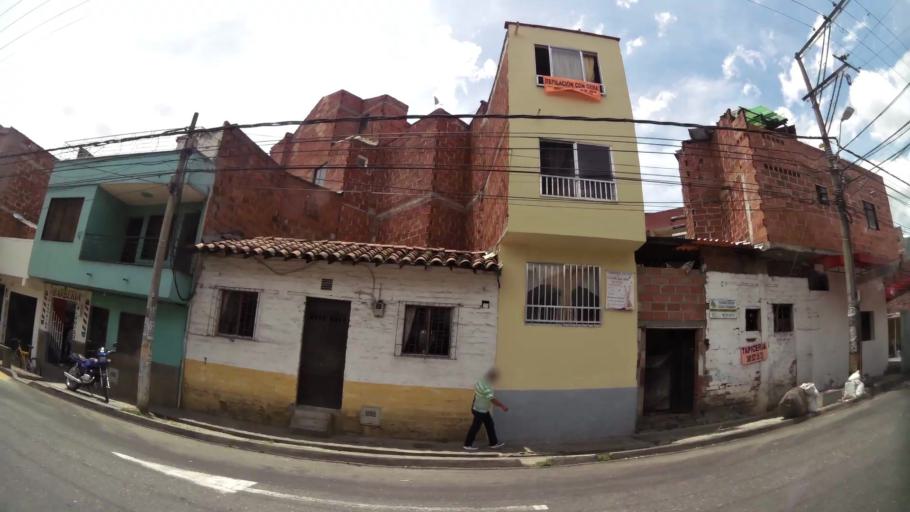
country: CO
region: Antioquia
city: Bello
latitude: 6.3409
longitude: -75.5601
